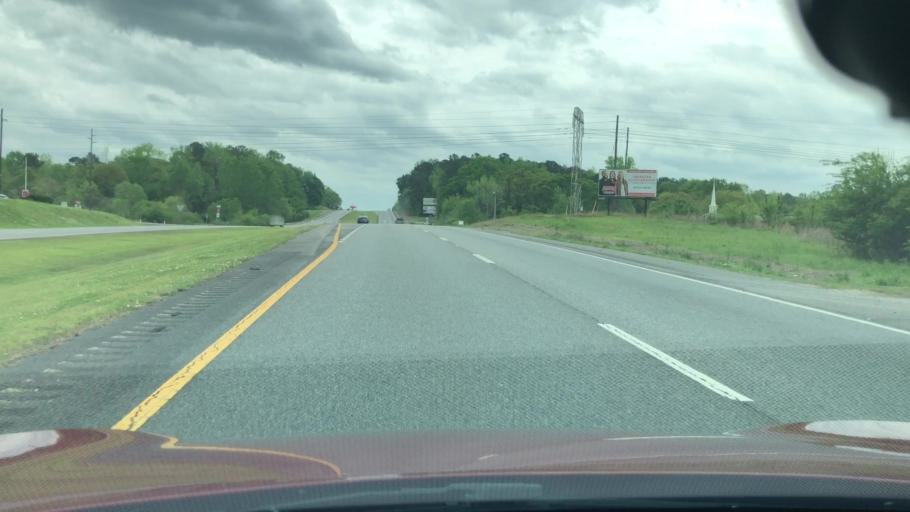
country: US
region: Alabama
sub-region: Tallapoosa County
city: Alexander City
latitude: 32.9494
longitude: -85.9861
